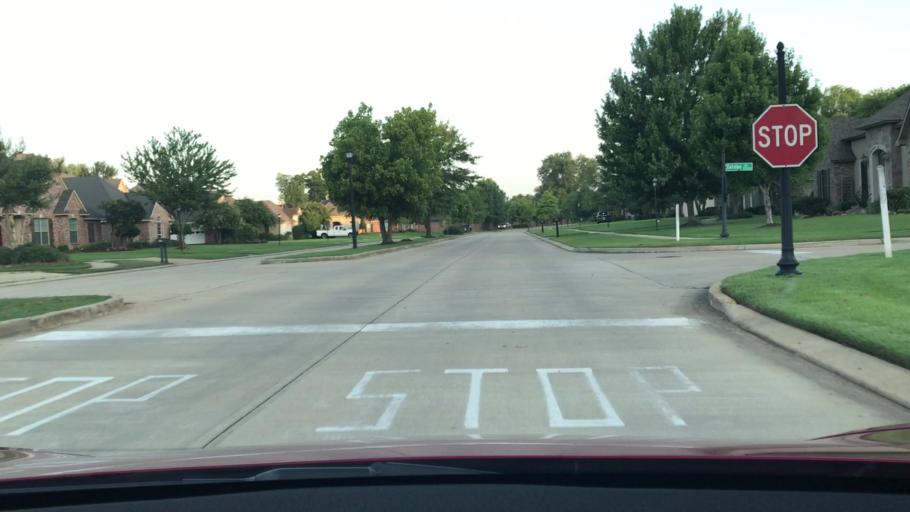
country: US
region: Louisiana
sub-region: Bossier Parish
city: Bossier City
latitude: 32.3973
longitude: -93.7073
